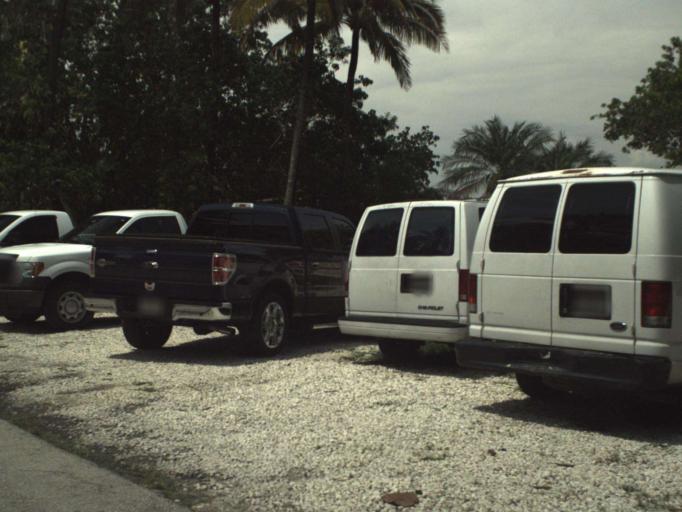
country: US
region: Florida
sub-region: Broward County
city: Lighthouse Point
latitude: 26.2670
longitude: -80.0806
